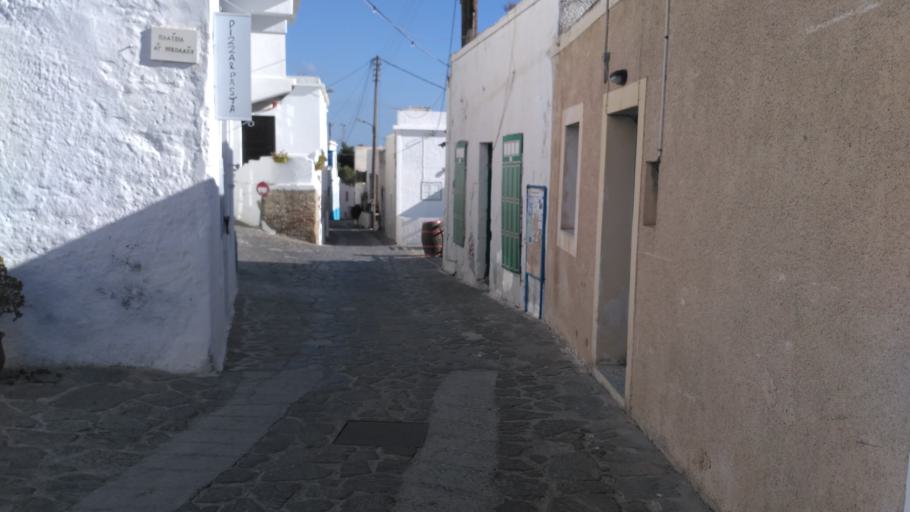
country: GR
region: South Aegean
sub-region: Nomos Kykladon
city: Milos
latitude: 36.7383
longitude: 24.4266
